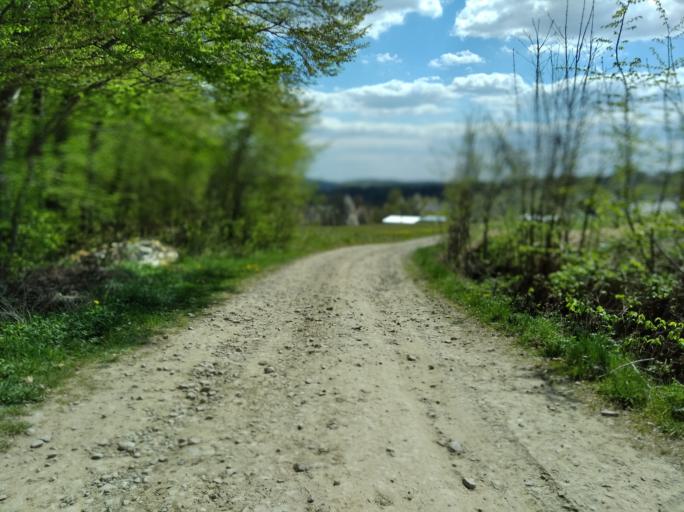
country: PL
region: Subcarpathian Voivodeship
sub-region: Powiat brzozowski
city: Golcowa
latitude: 49.7606
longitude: 22.0640
